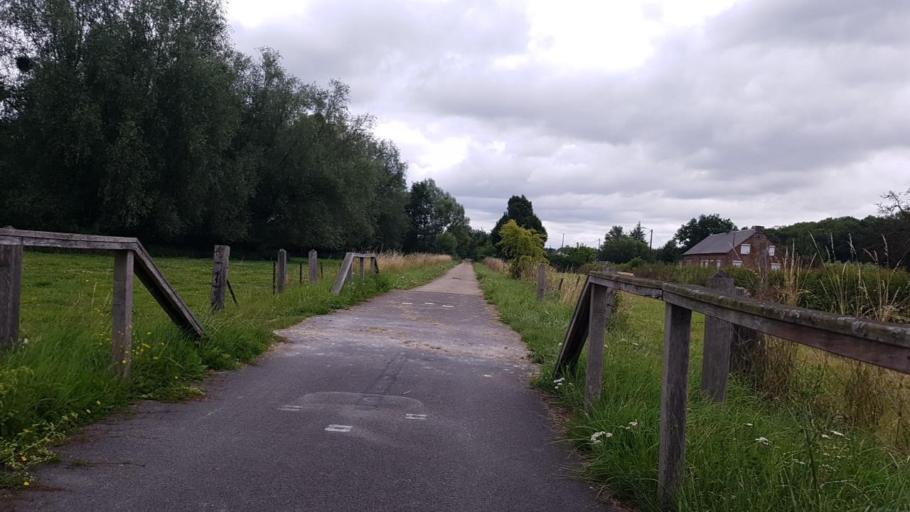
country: FR
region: Picardie
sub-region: Departement de l'Aisne
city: Buironfosse
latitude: 49.9046
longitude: 3.7972
